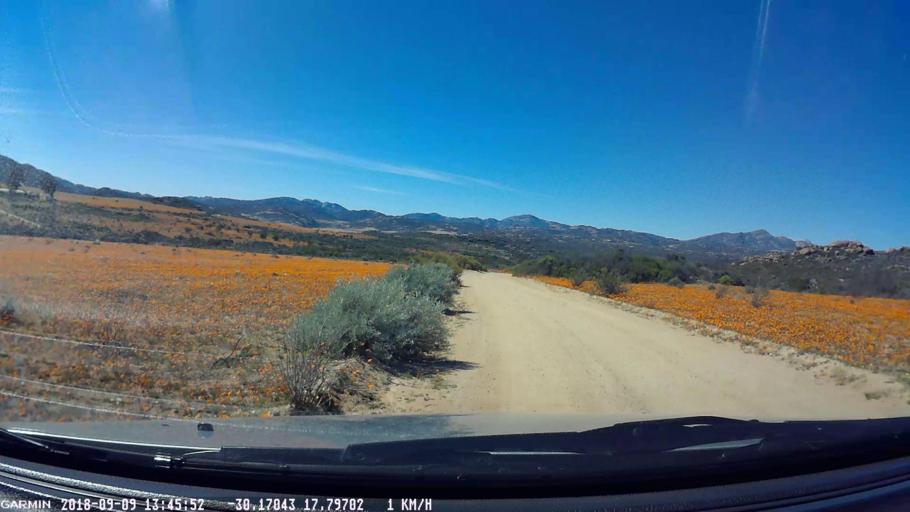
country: ZA
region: Northern Cape
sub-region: Namakwa District Municipality
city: Garies
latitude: -30.1704
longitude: 17.7966
